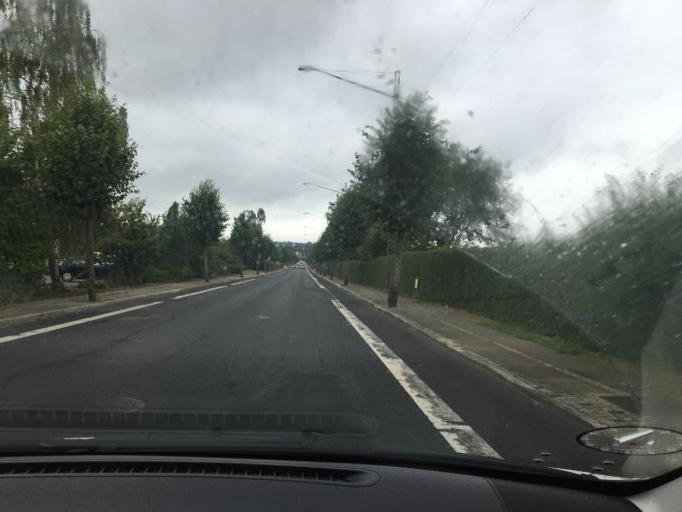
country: DK
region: South Denmark
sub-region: Middelfart Kommune
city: Middelfart
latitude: 55.4932
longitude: 9.7582
